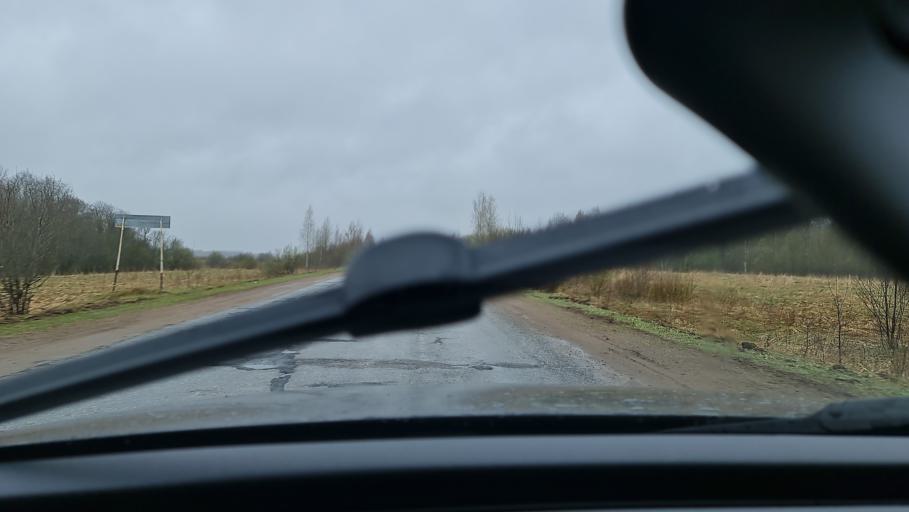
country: RU
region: Novgorod
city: Kresttsy
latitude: 58.0099
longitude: 32.7757
